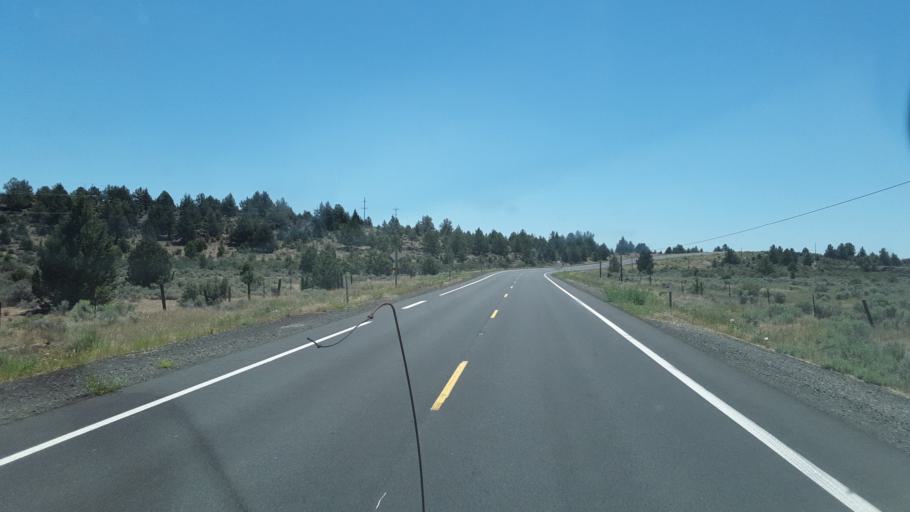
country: US
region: California
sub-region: Siskiyou County
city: Tulelake
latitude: 41.7109
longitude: -121.2836
